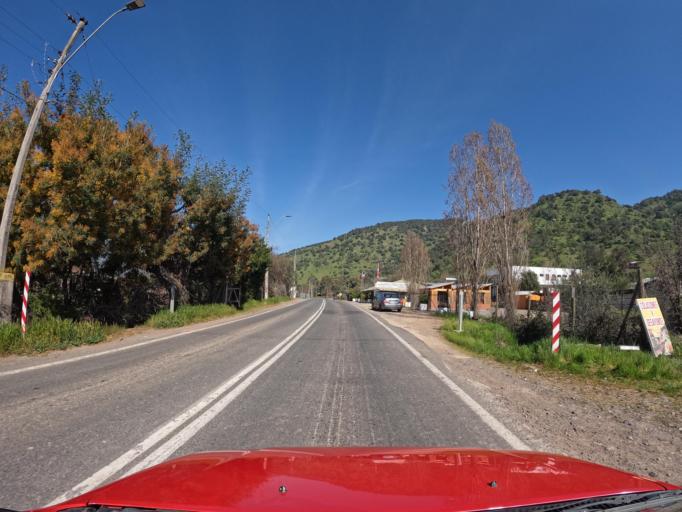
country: CL
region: Maule
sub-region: Provincia de Curico
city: Rauco
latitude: -34.9660
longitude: -71.3770
